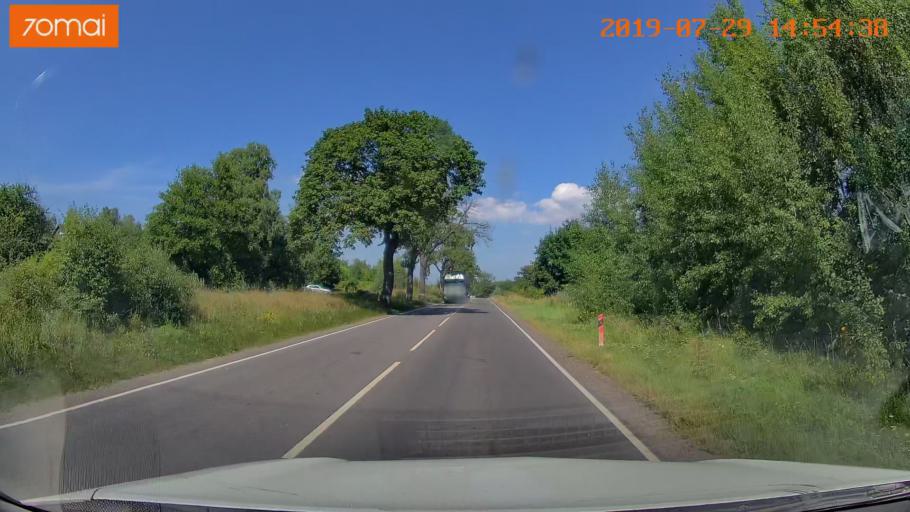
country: RU
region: Kaliningrad
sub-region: Gorod Kaliningrad
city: Baltiysk
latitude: 54.6756
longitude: 19.9260
